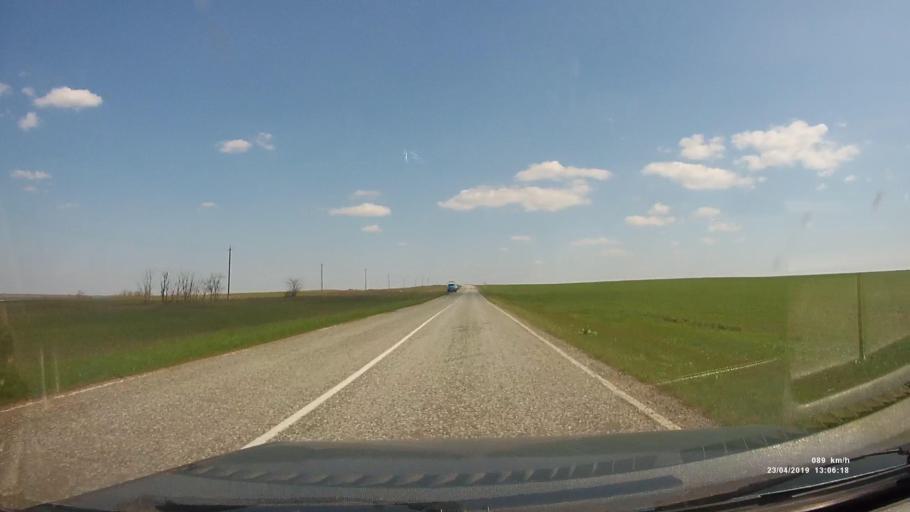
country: RU
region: Kalmykiya
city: Yashalta
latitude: 46.5918
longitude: 42.7388
